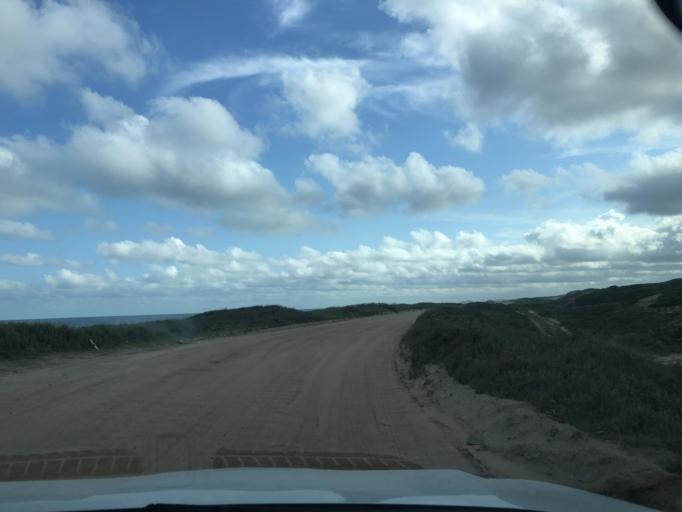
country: BR
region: Santa Catarina
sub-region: Sao Francisco Do Sul
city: Sao Francisco do Sul
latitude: -26.2634
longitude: -48.5208
